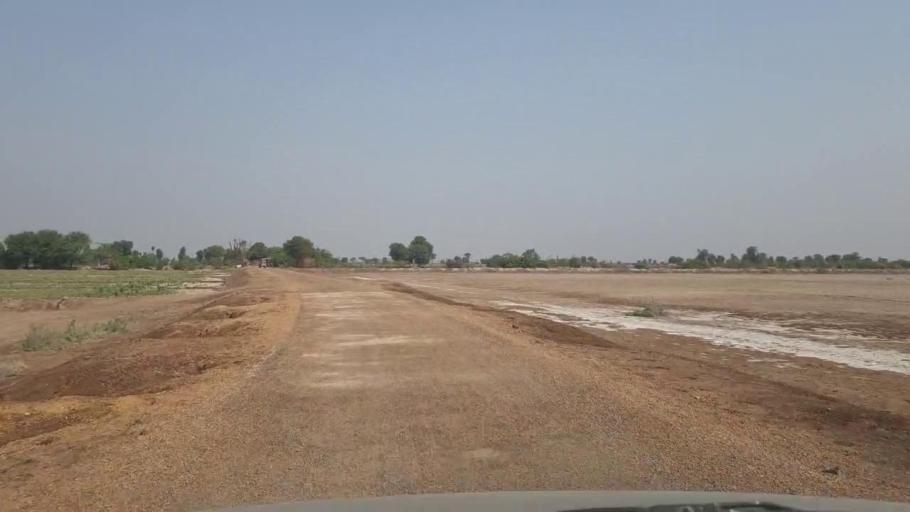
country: PK
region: Sindh
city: Chor
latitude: 25.4837
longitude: 69.7408
